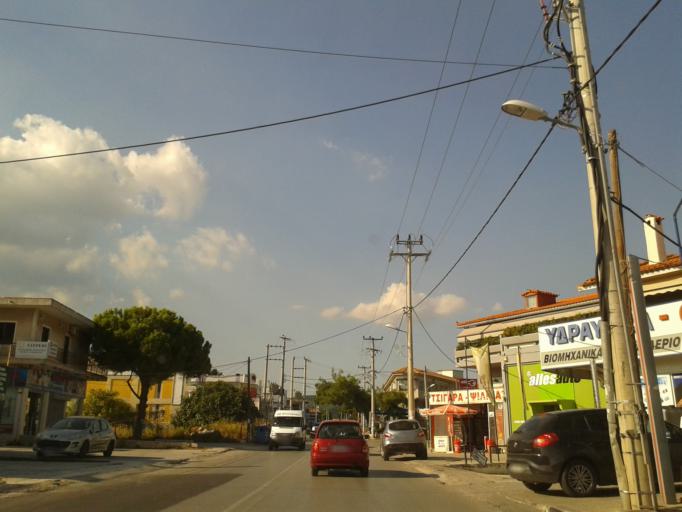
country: GR
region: Attica
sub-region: Nomarchia Anatolikis Attikis
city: Anoixi
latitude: 38.1374
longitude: 23.8556
